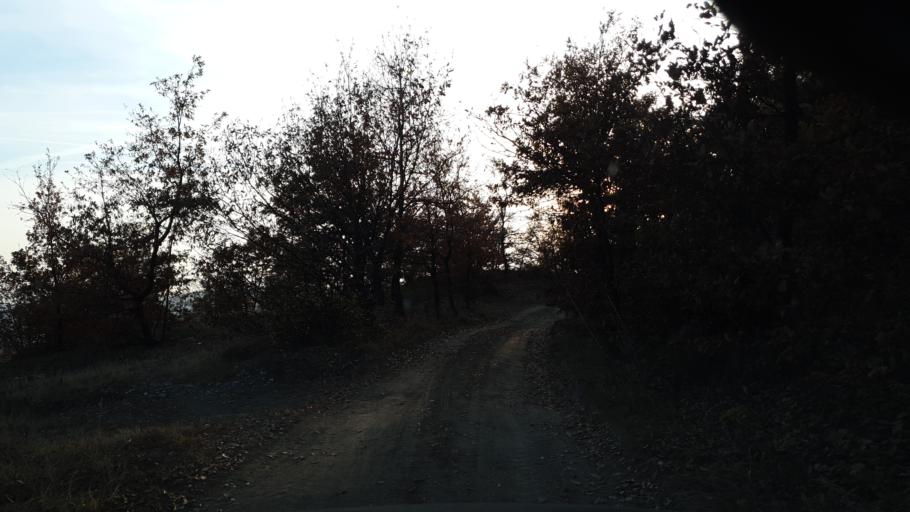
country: RS
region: Central Serbia
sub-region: Borski Okrug
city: Bor
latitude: 44.0731
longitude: 22.0709
